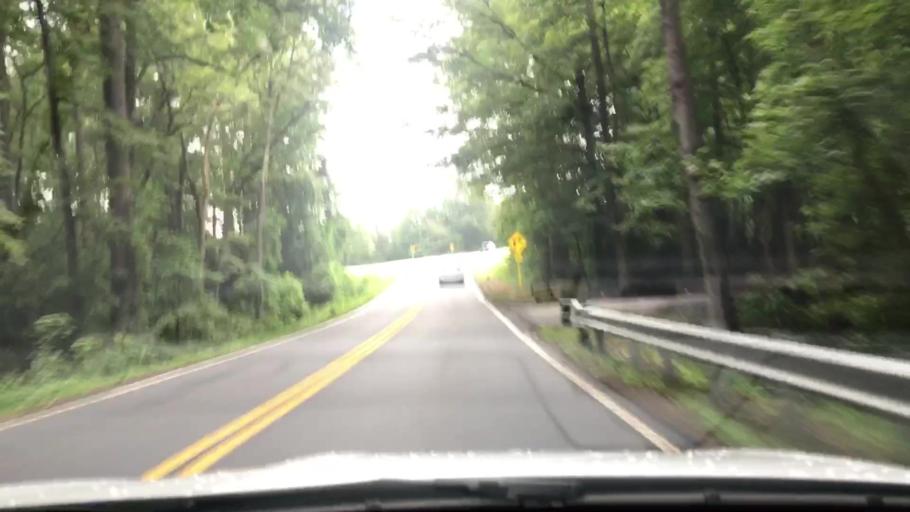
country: US
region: South Carolina
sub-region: Spartanburg County
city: Roebuck
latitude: 34.8351
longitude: -81.9662
